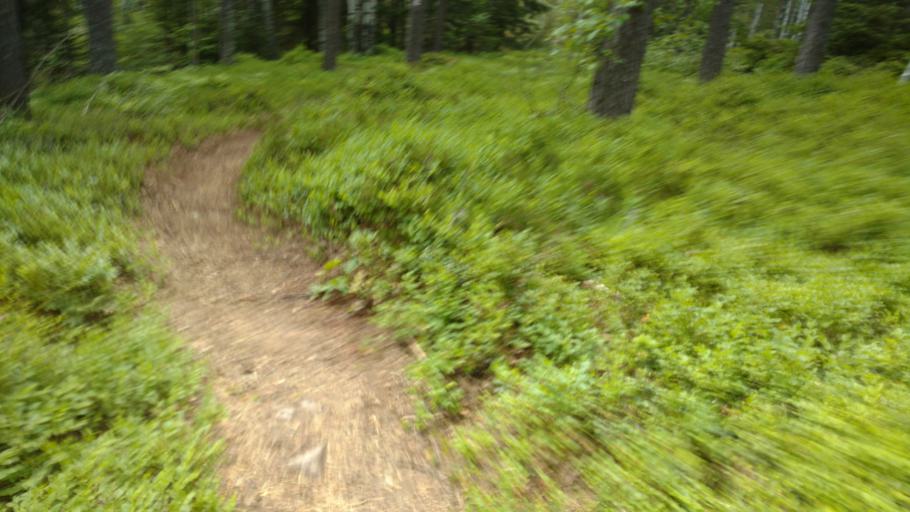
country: FI
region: Uusimaa
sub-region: Raaseporin
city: Pohja
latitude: 60.1129
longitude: 23.5535
